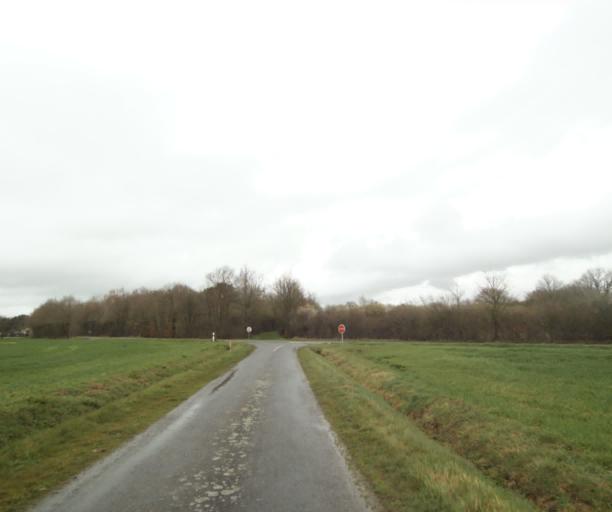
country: FR
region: Pays de la Loire
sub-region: Departement de la Loire-Atlantique
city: Bouvron
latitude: 47.4598
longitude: -1.8778
